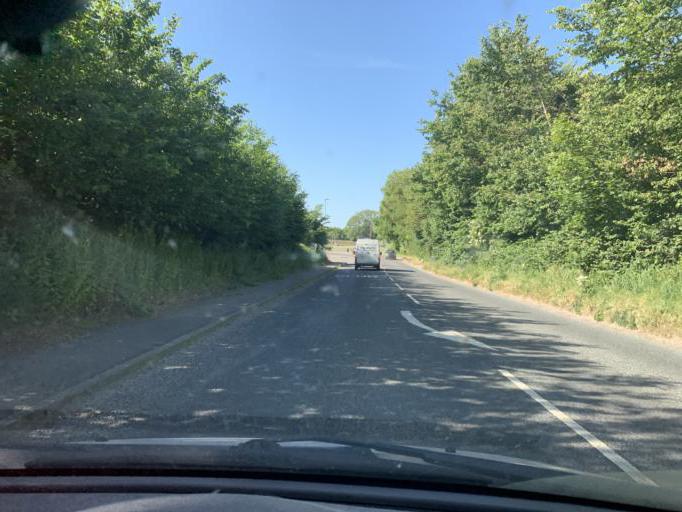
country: GB
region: England
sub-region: Wiltshire
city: Durnford
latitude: 51.1085
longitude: -1.7931
